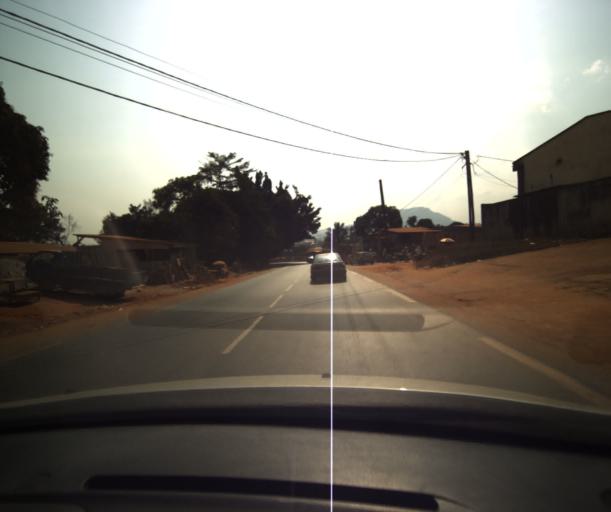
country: CM
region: Centre
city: Okoa
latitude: 3.9656
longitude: 11.5408
